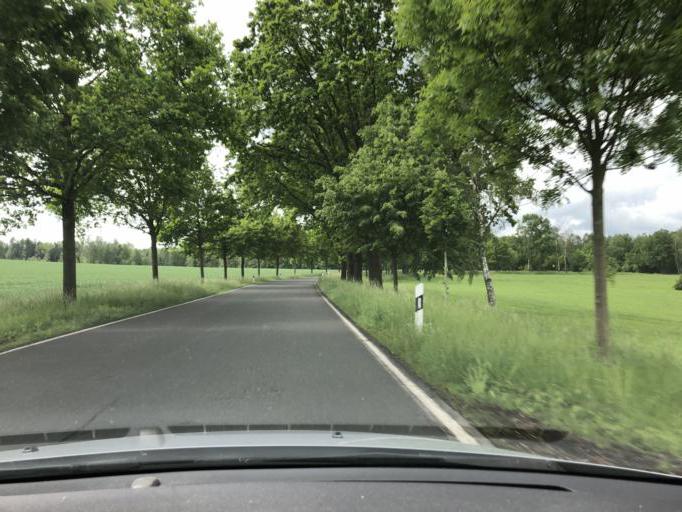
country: DE
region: Saxony
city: Waldenburg
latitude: 50.8568
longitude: 12.5992
